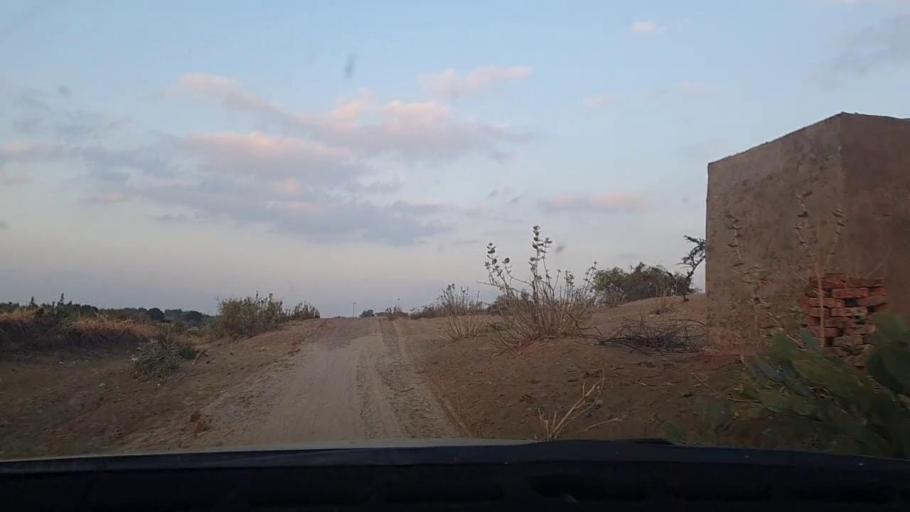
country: PK
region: Sindh
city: Tando Mittha Khan
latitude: 25.9496
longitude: 69.3401
